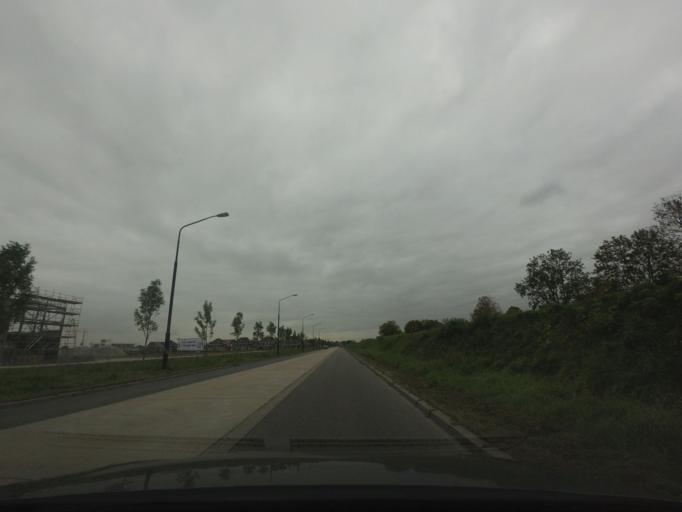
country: NL
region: North Holland
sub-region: Gemeente Heerhugowaard
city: Heerhugowaard
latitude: 52.6713
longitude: 4.8606
